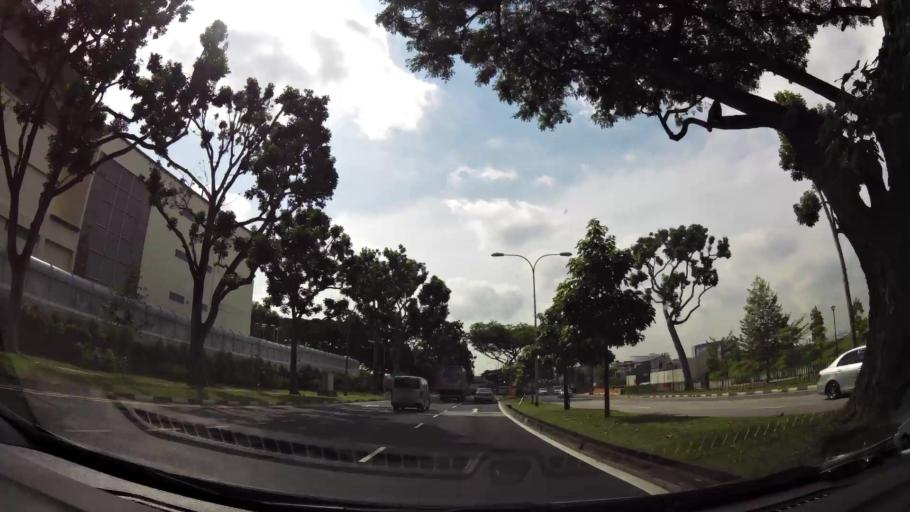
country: SG
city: Singapore
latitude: 1.3467
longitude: 103.8907
